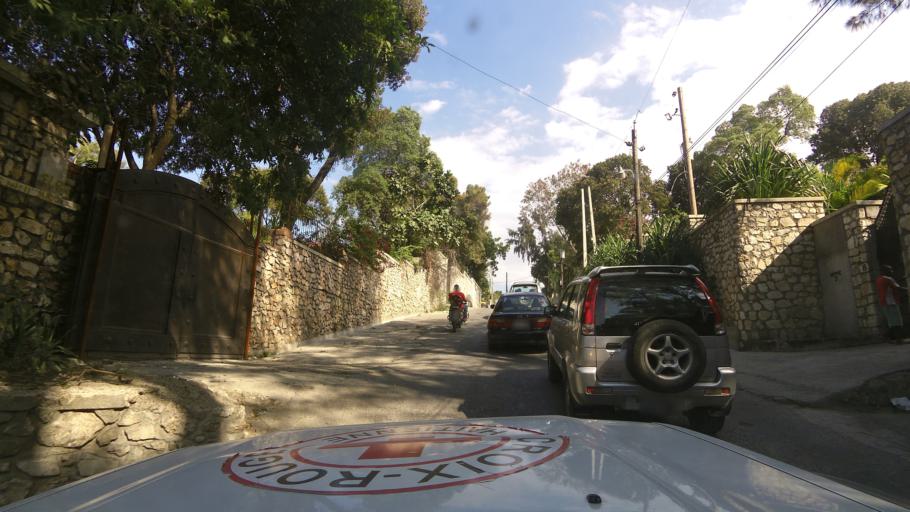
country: HT
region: Ouest
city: Petionville
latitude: 18.5319
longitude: -72.2841
